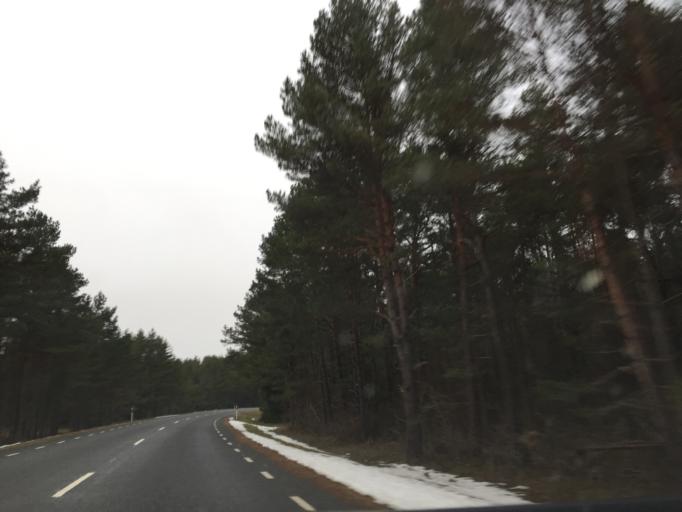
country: EE
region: Saare
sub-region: Kuressaare linn
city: Kuressaare
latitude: 58.5549
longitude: 22.3172
